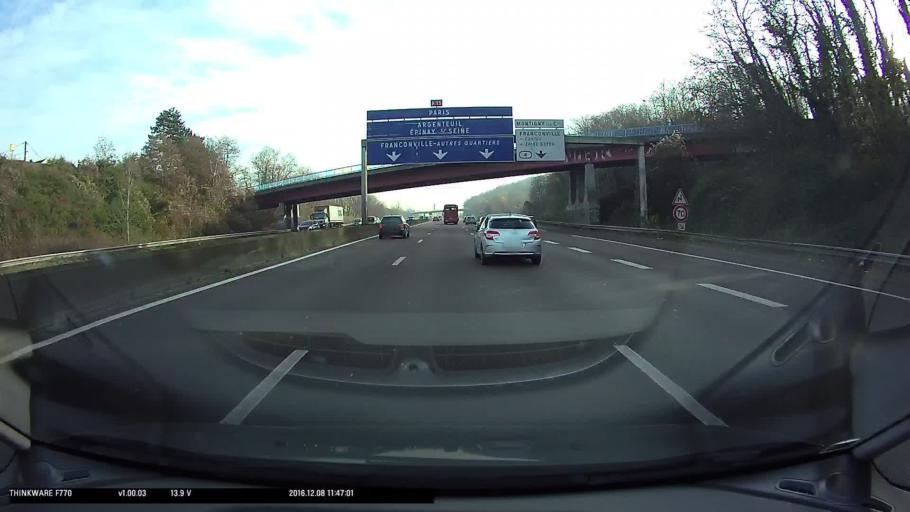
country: FR
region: Ile-de-France
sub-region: Departement du Val-d'Oise
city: Montigny-les-Cormeilles
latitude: 48.9906
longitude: 2.1944
